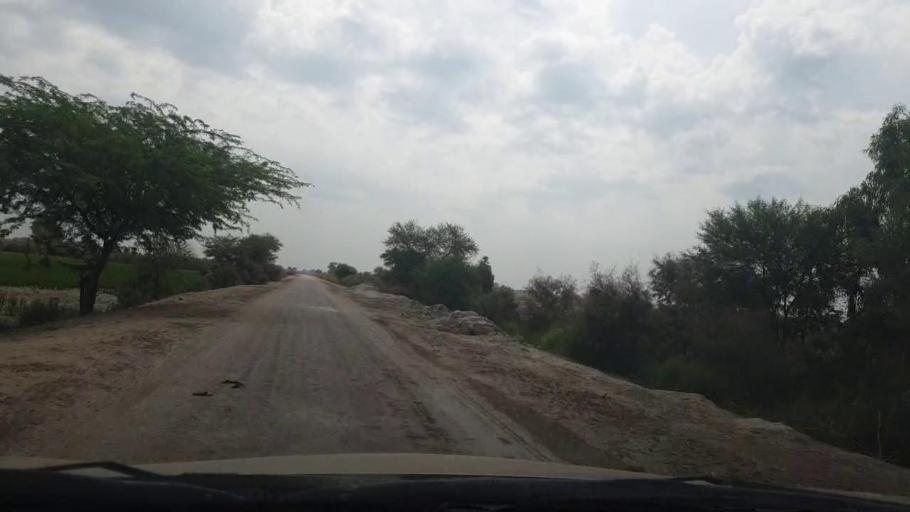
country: PK
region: Sindh
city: Miro Khan
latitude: 27.6966
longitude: 68.2075
